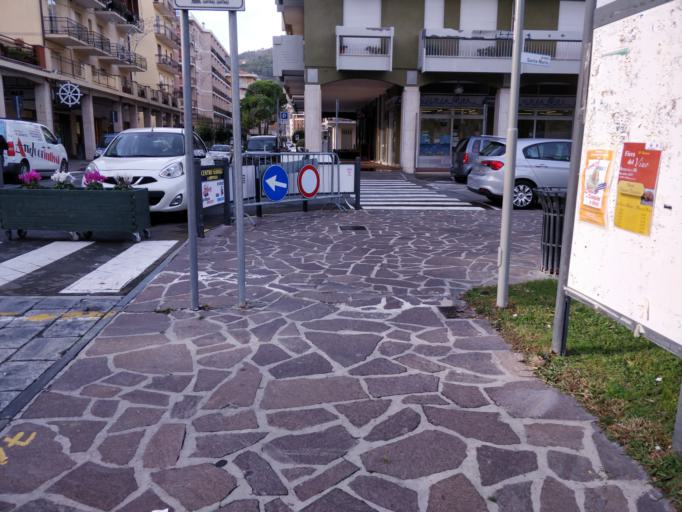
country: IT
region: Liguria
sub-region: Provincia di Savona
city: Andora
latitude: 43.9515
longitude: 8.1465
